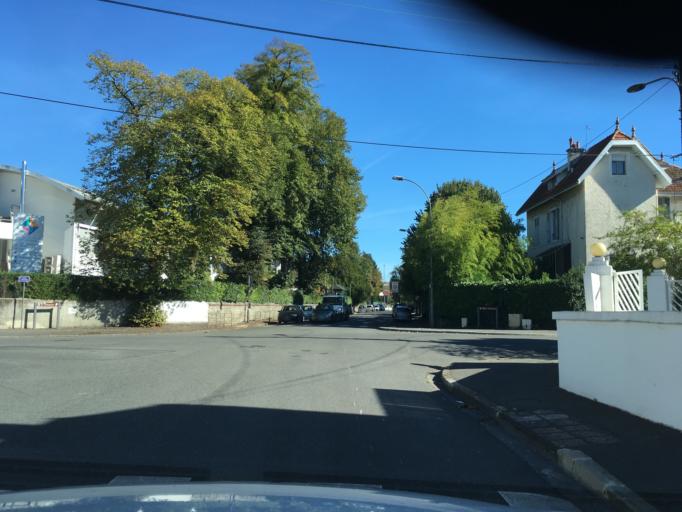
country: FR
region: Aquitaine
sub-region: Departement des Pyrenees-Atlantiques
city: Pau
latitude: 43.3138
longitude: -0.3761
